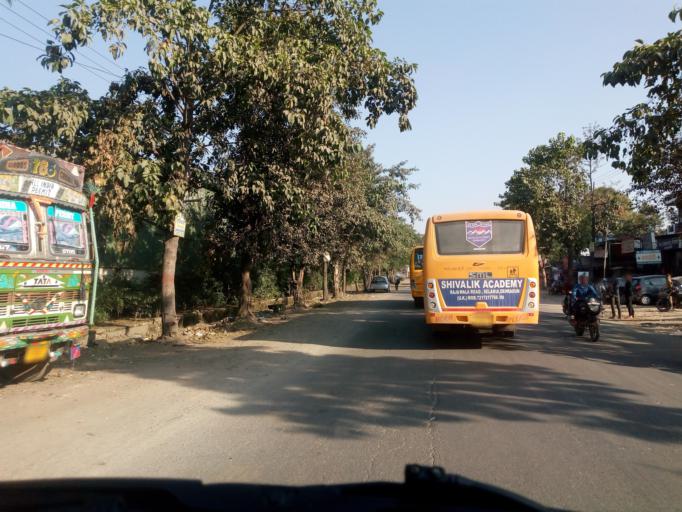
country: IN
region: Uttarakhand
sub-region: Dehradun
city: Vikasnagar
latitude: 30.3584
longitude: 77.8506
